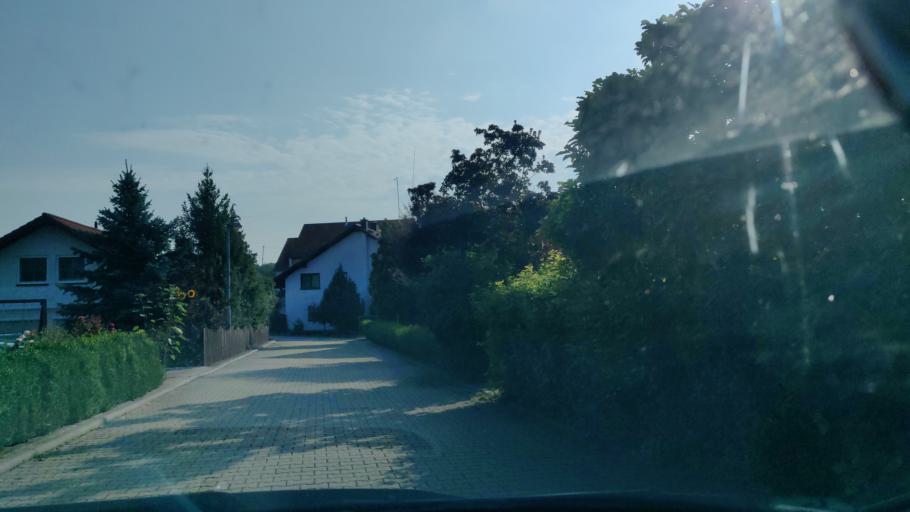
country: DE
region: Saxony
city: Bad Lausick
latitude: 51.1360
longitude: 12.6483
